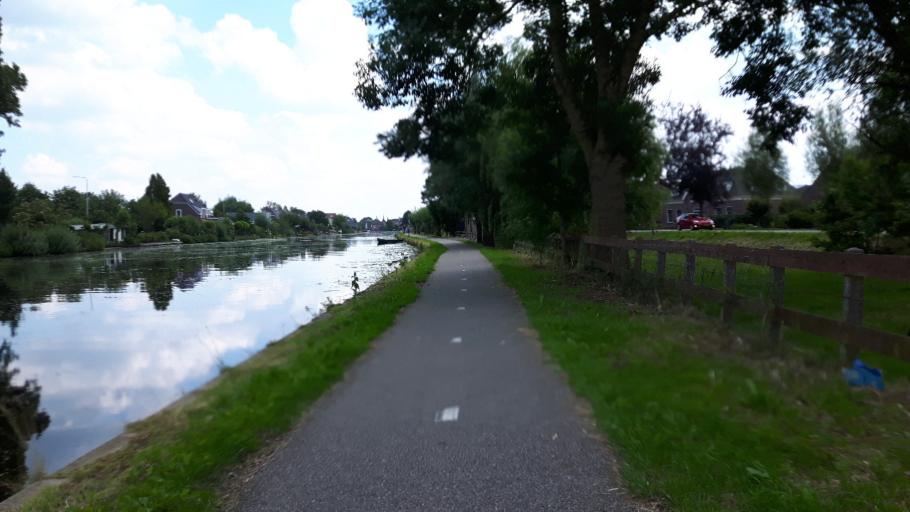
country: NL
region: South Holland
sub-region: Bodegraven-Reeuwijk
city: Bodegraven
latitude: 52.0817
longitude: 4.8031
